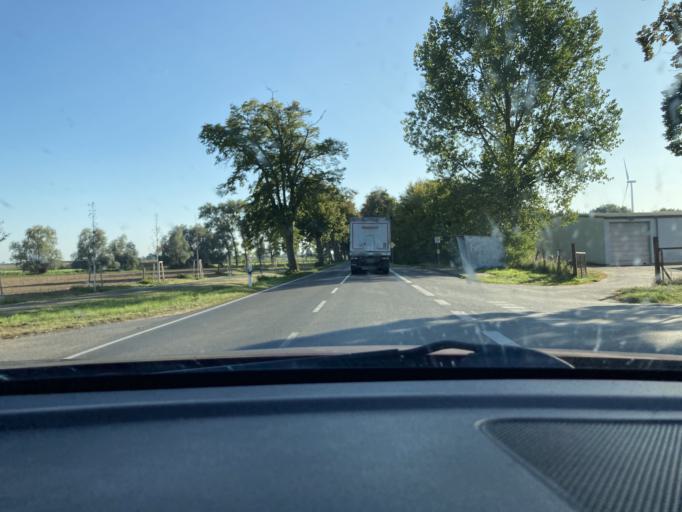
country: DE
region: Mecklenburg-Vorpommern
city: Alt-Sanitz
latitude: 53.7835
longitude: 13.6596
